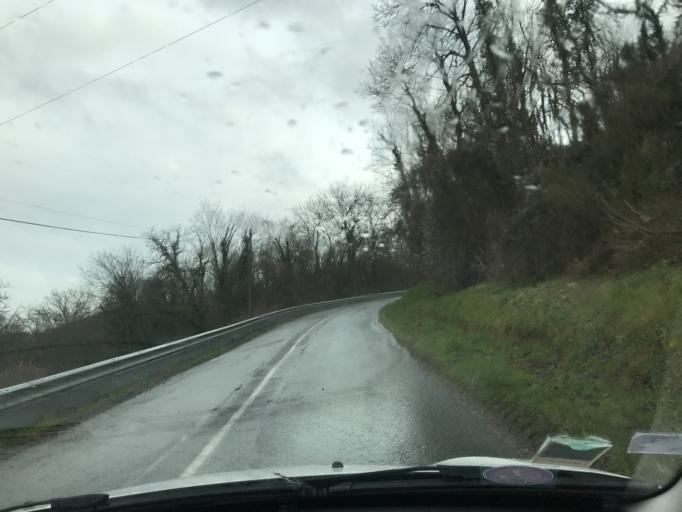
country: FR
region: Picardie
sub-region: Departement de l'Aisne
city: Billy-sur-Aisne
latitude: 49.3472
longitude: 3.3860
